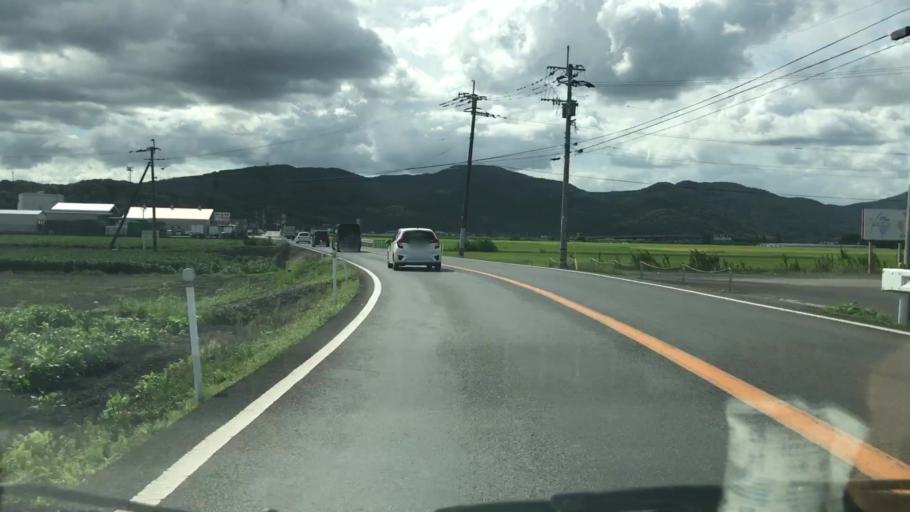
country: JP
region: Saga Prefecture
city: Kashima
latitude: 33.1398
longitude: 130.1322
